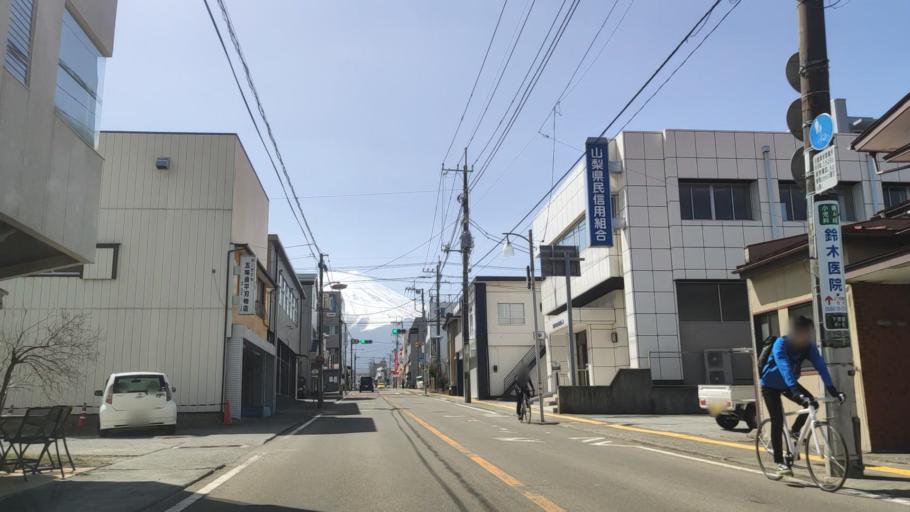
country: JP
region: Yamanashi
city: Fujikawaguchiko
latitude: 35.4885
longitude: 138.8014
